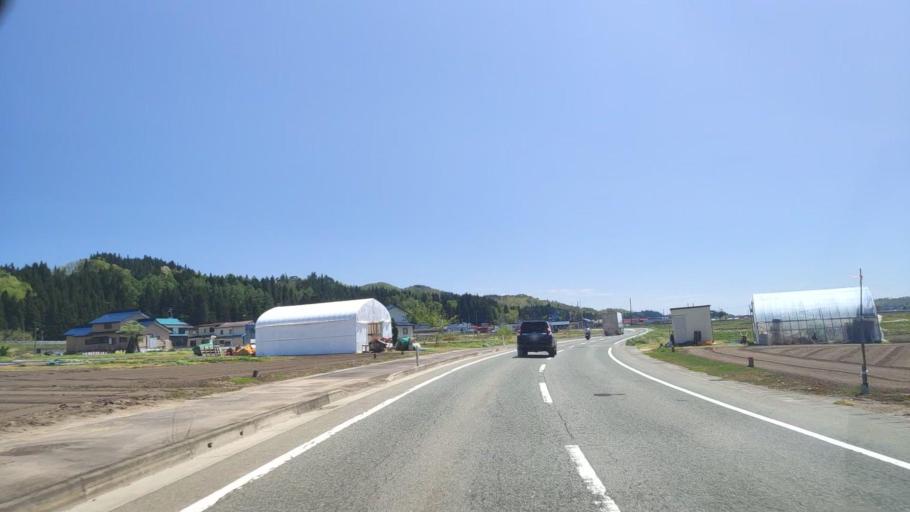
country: JP
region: Yamagata
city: Obanazawa
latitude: 38.5593
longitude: 140.4002
